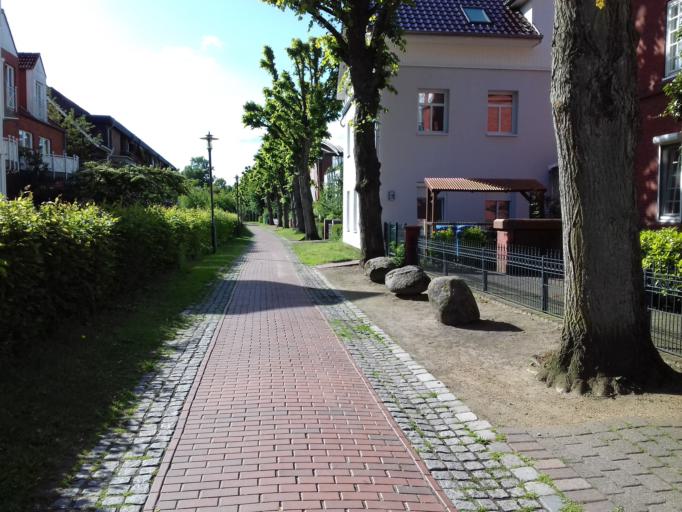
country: DE
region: Schleswig-Holstein
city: Neumunster
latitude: 54.0698
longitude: 9.9904
